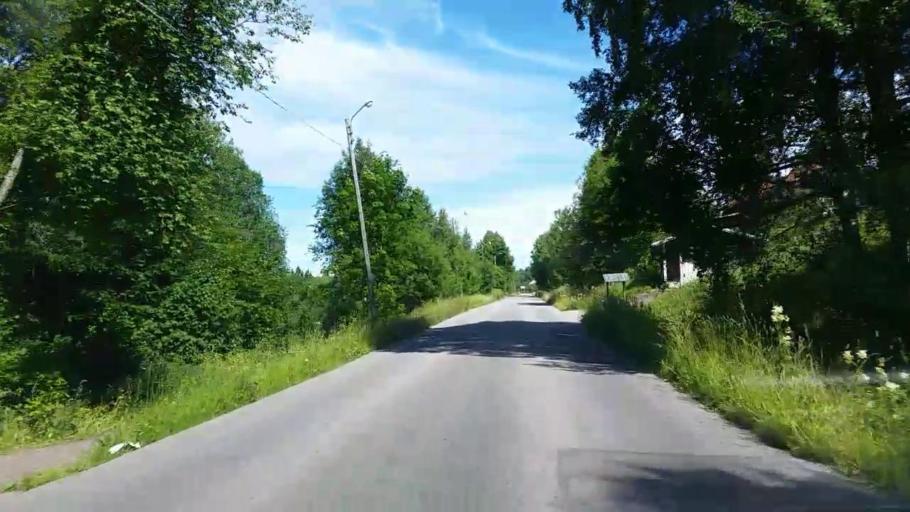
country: SE
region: Dalarna
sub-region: Rattviks Kommun
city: Raettvik
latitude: 60.8836
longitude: 15.1302
